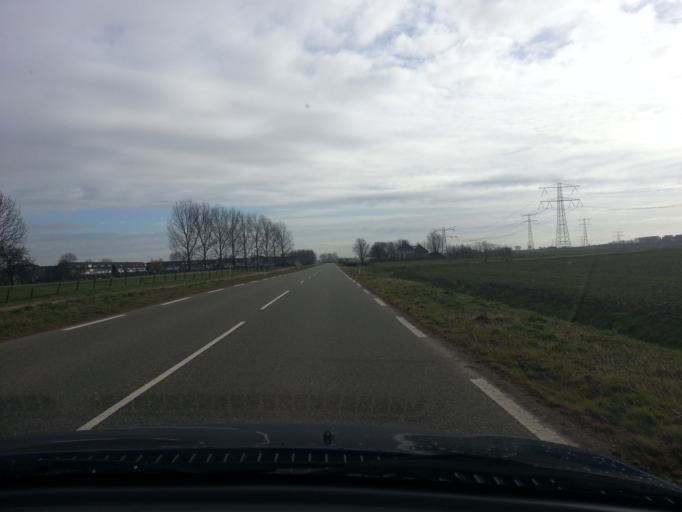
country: NL
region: South Holland
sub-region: Gemeente Spijkenisse
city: Spijkenisse
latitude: 51.8234
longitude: 4.3233
